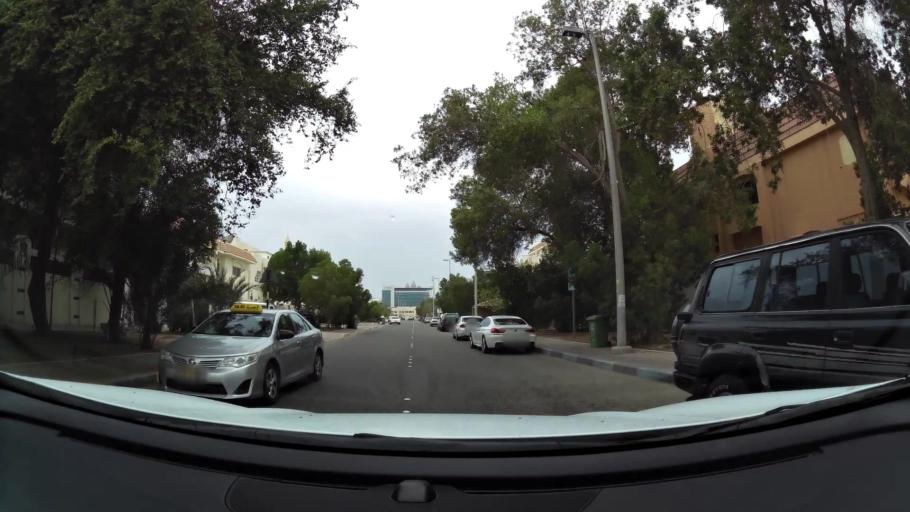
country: AE
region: Abu Dhabi
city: Abu Dhabi
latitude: 24.4803
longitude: 54.3836
